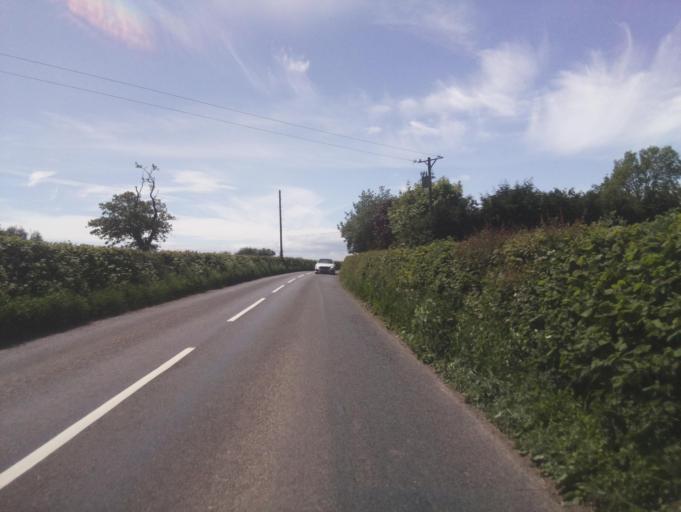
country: GB
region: Wales
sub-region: Monmouthshire
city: Mitchel Troy
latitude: 51.7357
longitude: -2.7365
